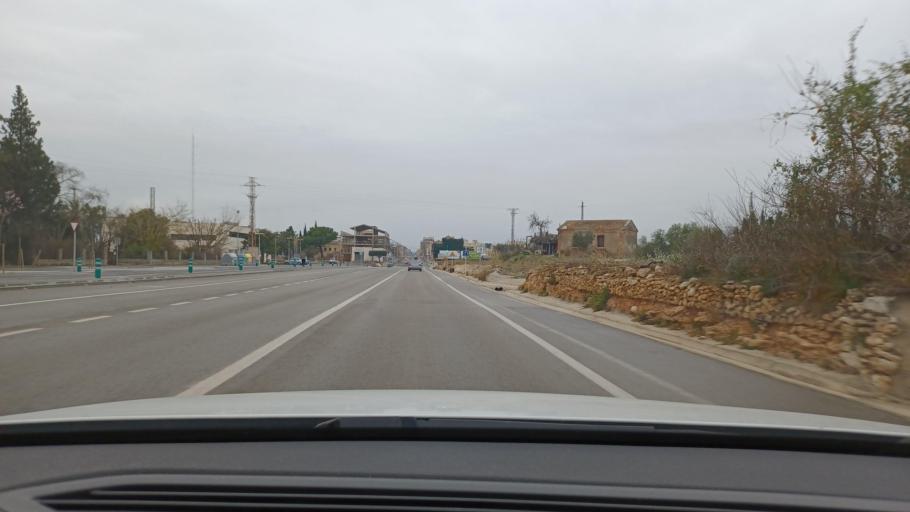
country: ES
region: Catalonia
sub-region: Provincia de Tarragona
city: Camarles
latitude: 40.7470
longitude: 0.6213
